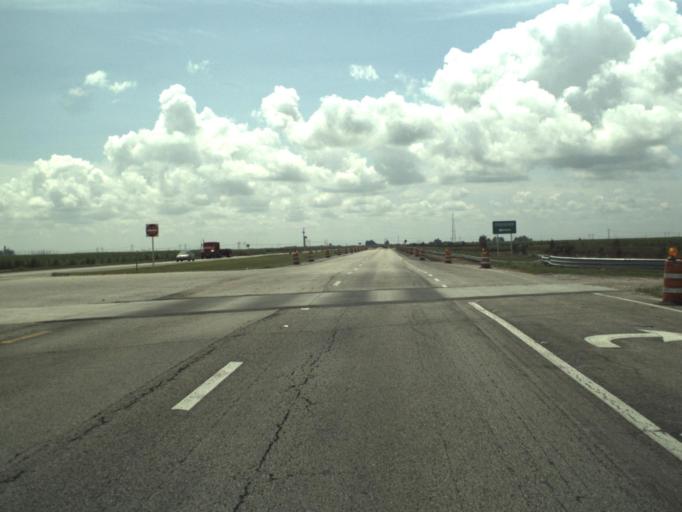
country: US
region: Florida
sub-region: Palm Beach County
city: Loxahatchee Groves
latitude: 26.7084
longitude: -80.4173
